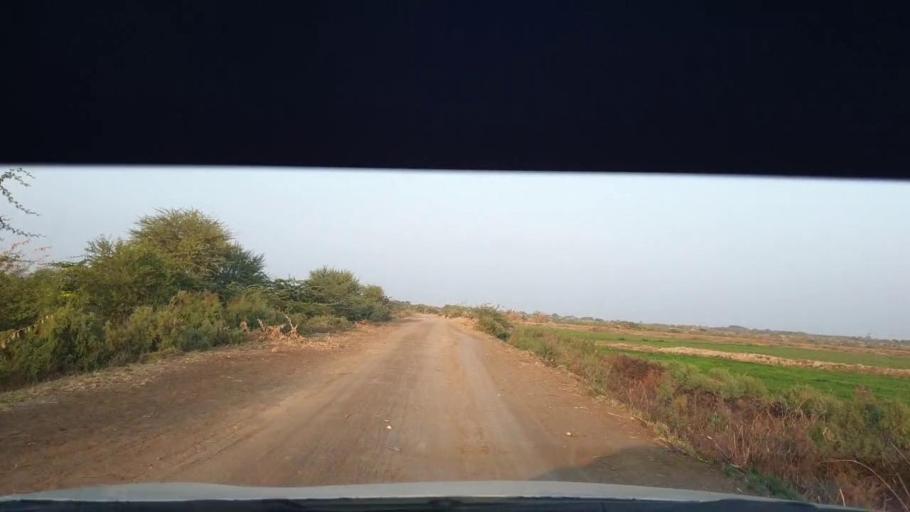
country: PK
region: Sindh
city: Berani
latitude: 25.7467
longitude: 68.9738
